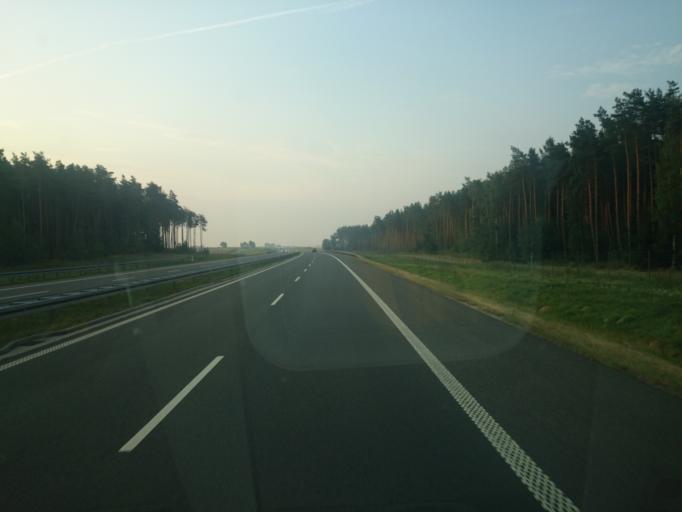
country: PL
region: West Pomeranian Voivodeship
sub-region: Powiat pyrzycki
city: Bielice
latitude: 53.2157
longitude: 14.6554
